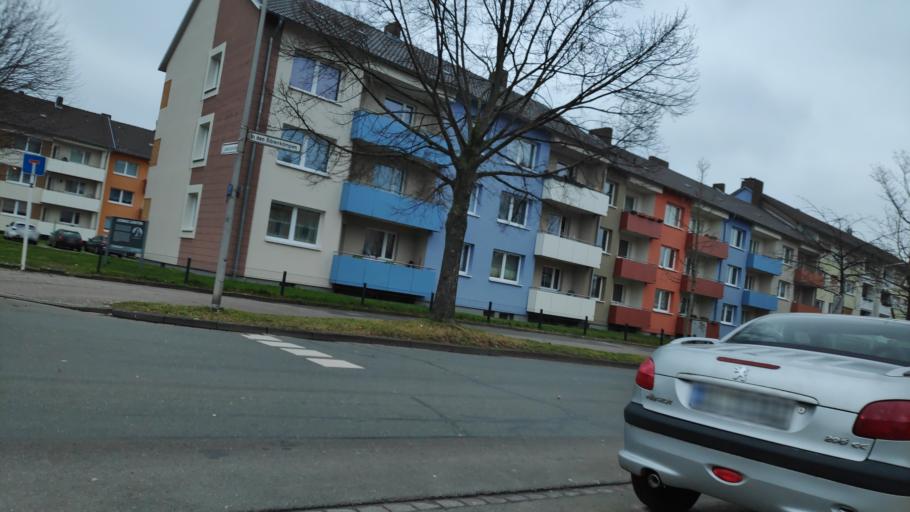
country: DE
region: North Rhine-Westphalia
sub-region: Regierungsbezirk Detmold
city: Minden
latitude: 52.3032
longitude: 8.8921
